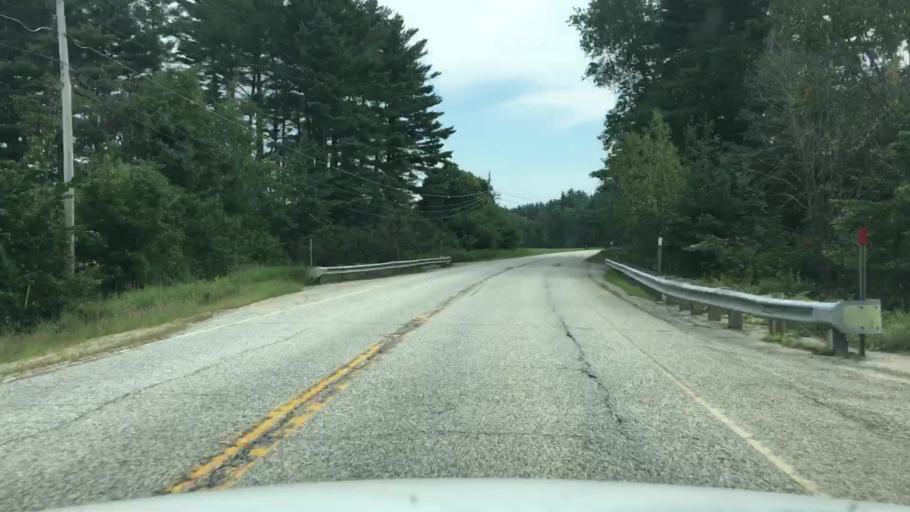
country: US
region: Maine
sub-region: Oxford County
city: Rumford
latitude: 44.6108
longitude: -70.7362
